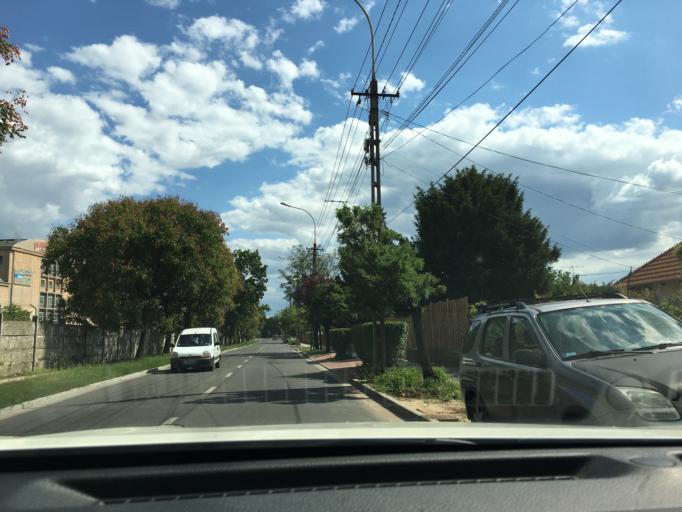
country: HU
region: Budapest
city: Budapest XVI. keruelet
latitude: 47.5194
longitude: 19.1887
